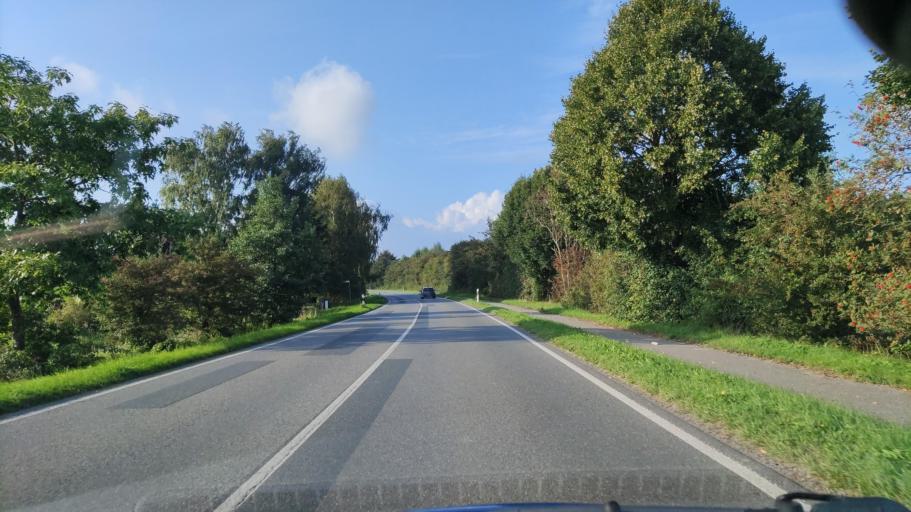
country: DE
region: Schleswig-Holstein
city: Stockelsdorf
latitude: 53.9543
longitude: 10.6203
